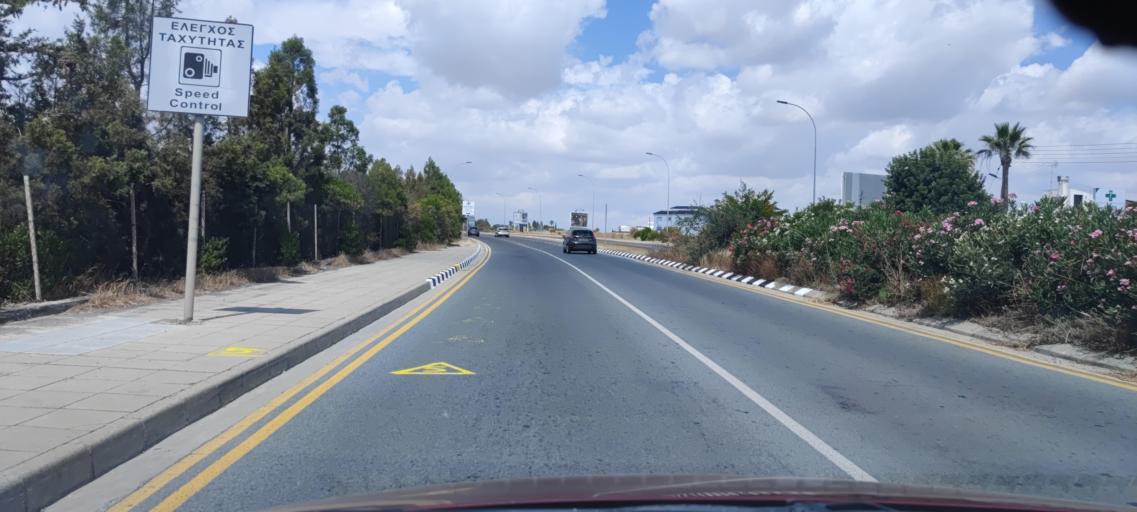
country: CY
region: Lefkosia
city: Nicosia
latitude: 35.1288
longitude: 33.3623
